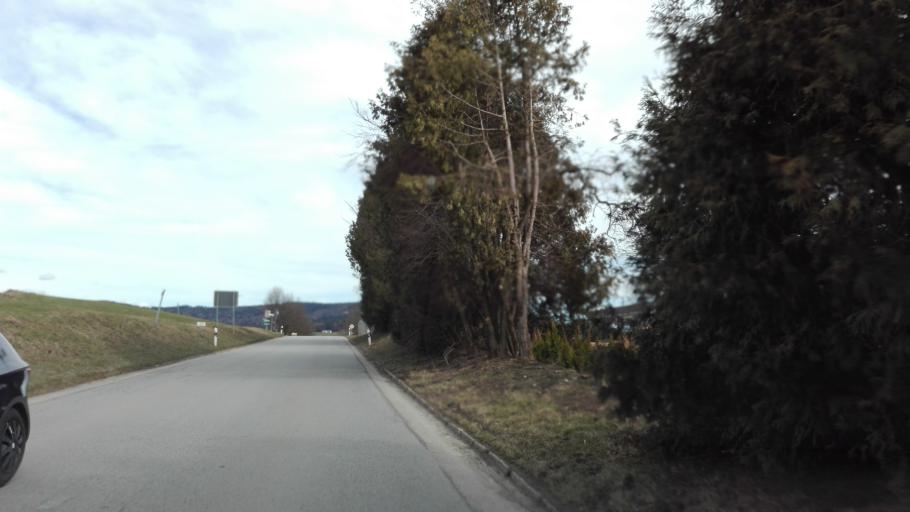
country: DE
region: Bavaria
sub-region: Lower Bavaria
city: Hauzenberg
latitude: 48.6298
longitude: 13.6422
